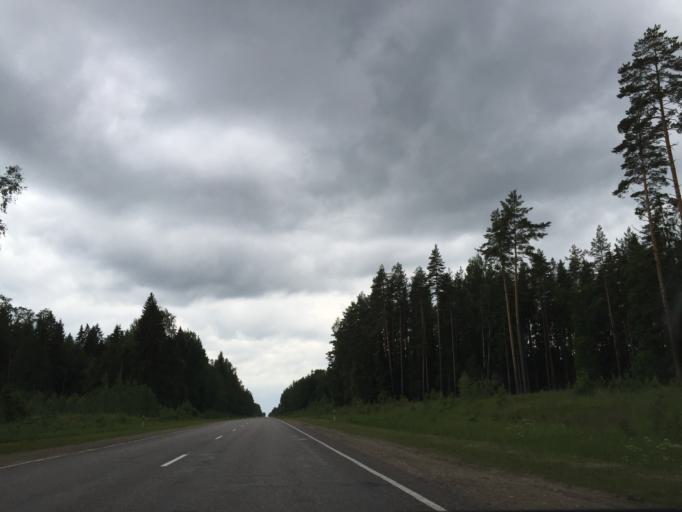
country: LV
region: Smiltene
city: Smiltene
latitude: 57.4084
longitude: 26.0573
